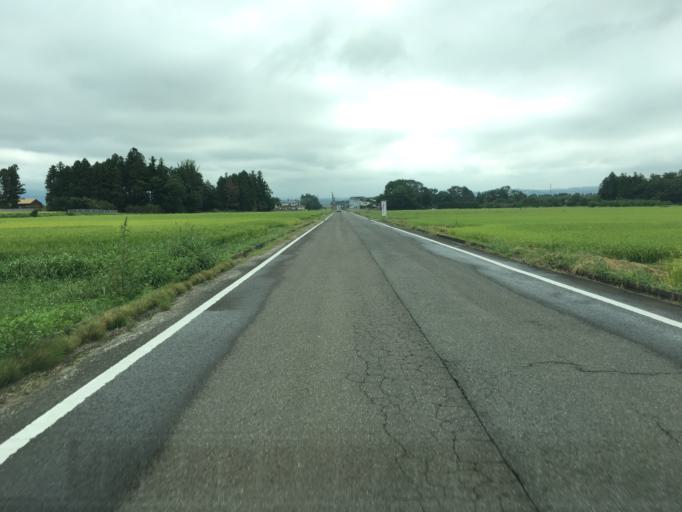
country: JP
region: Fukushima
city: Fukushima-shi
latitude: 37.7645
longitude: 140.3908
